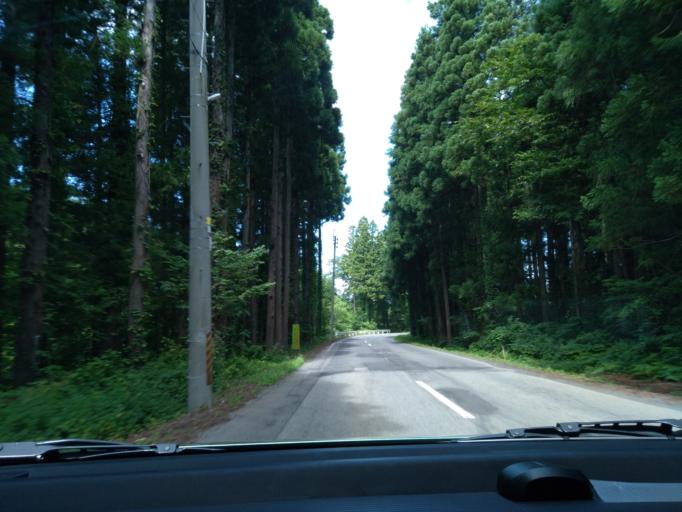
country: JP
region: Akita
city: Kakunodatemachi
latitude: 39.5985
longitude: 140.5767
